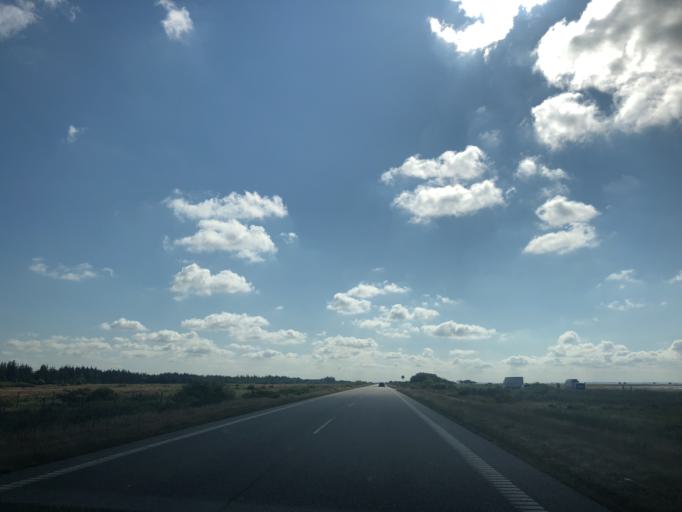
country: DK
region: North Denmark
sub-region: Vesthimmerland Kommune
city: Logstor
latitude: 57.0243
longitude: 9.0192
